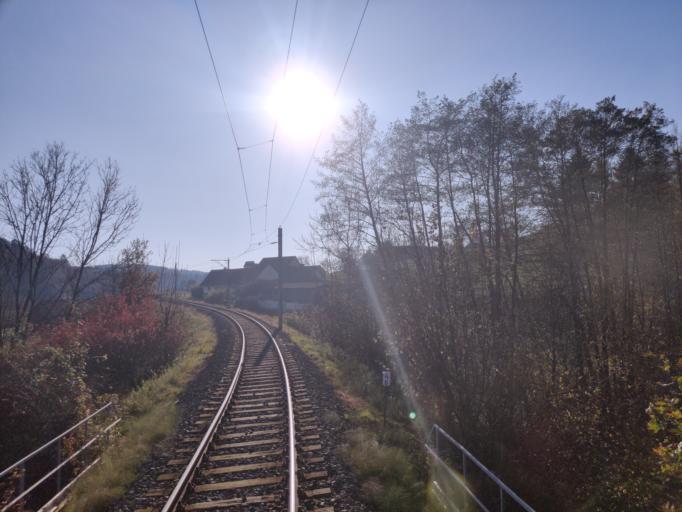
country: AT
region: Styria
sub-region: Politischer Bezirk Suedoststeiermark
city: Feldbach
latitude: 46.9352
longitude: 15.8660
